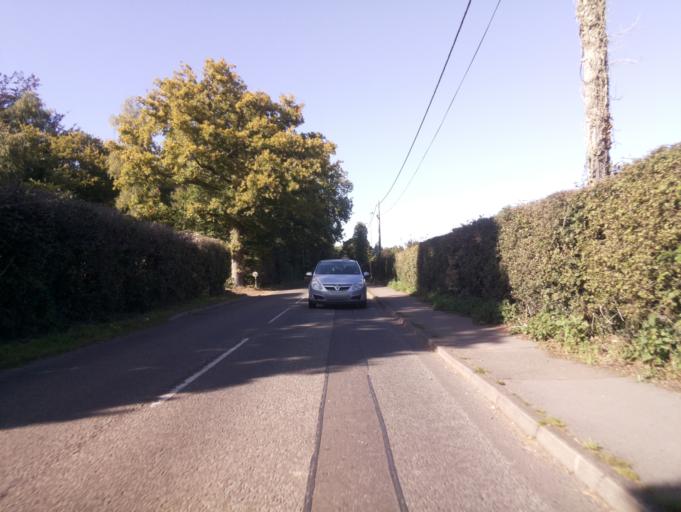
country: GB
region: England
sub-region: West Berkshire
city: Cold Ash
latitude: 51.4322
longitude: -1.2691
